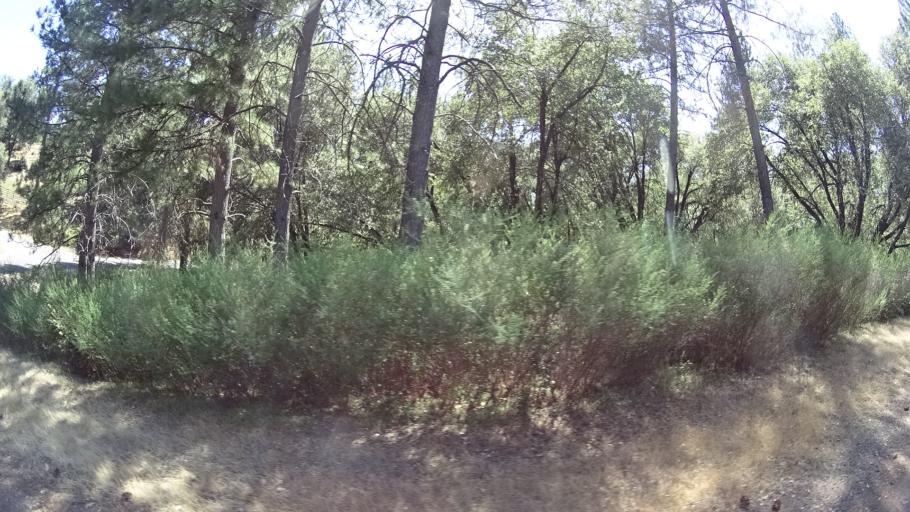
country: US
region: California
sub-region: Calaveras County
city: Murphys
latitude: 38.1709
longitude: -120.4664
